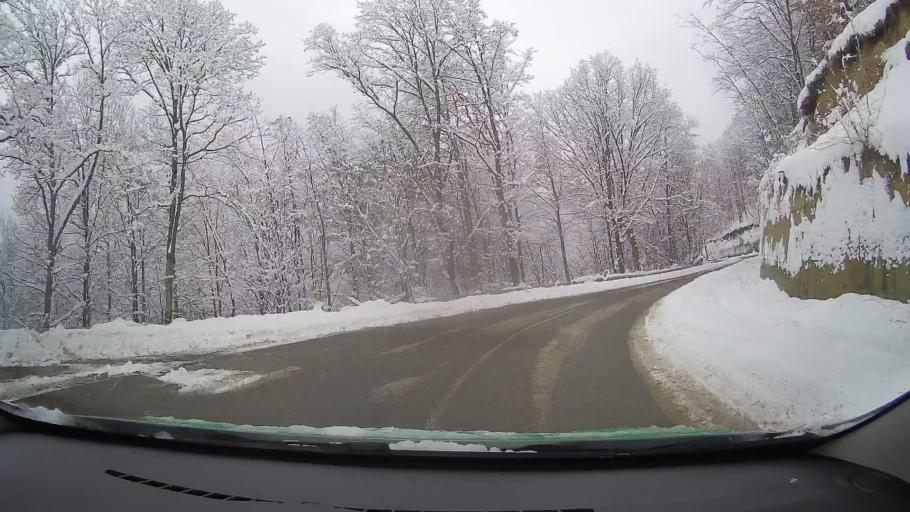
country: RO
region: Alba
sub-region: Comuna Sugag
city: Dobra
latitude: 45.7631
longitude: 23.6626
